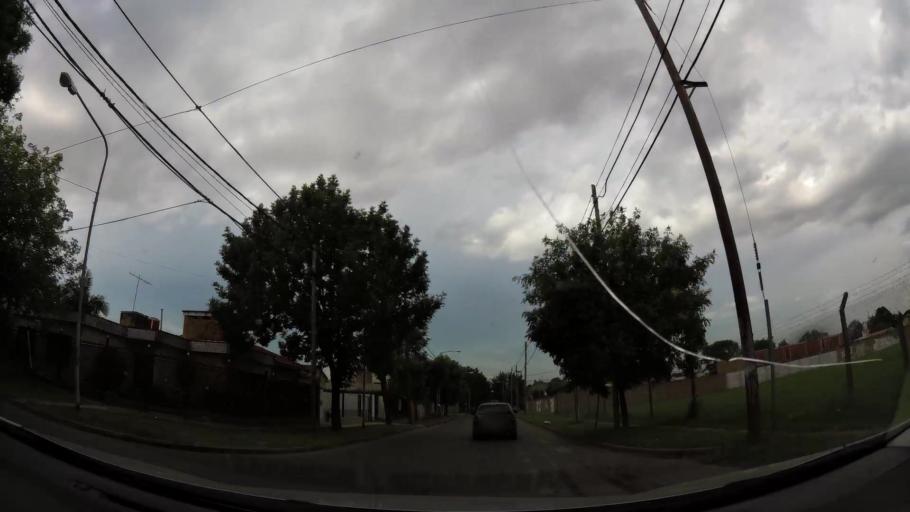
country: AR
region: Buenos Aires
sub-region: Partido de Tigre
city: Tigre
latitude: -34.4675
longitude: -58.6533
